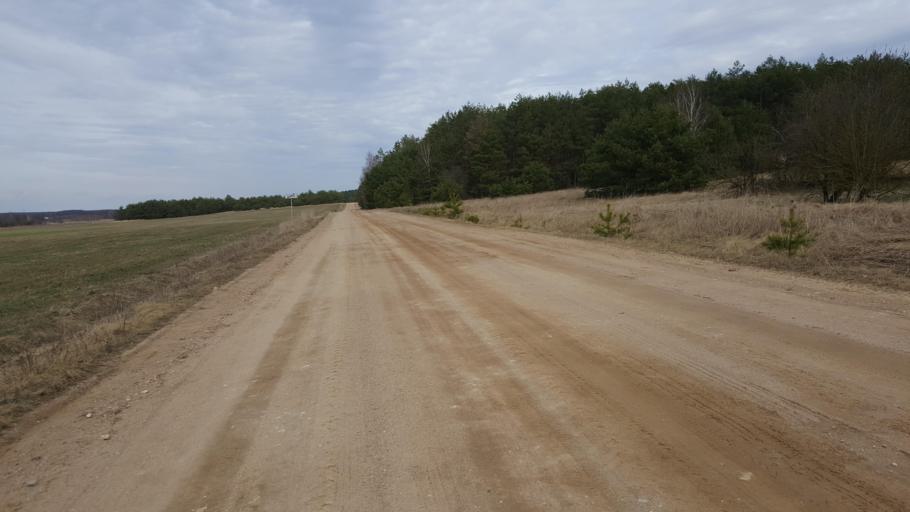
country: BY
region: Brest
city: Kamyanyets
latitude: 52.3748
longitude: 23.9844
